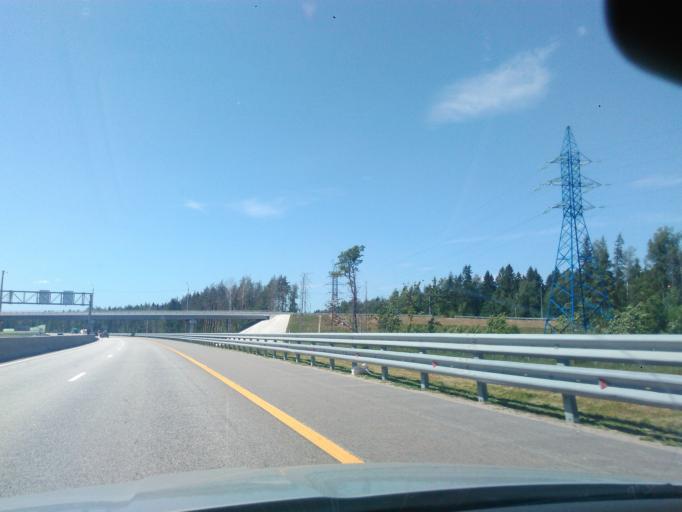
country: RU
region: Moskovskaya
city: Peshki
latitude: 56.1384
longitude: 37.0969
